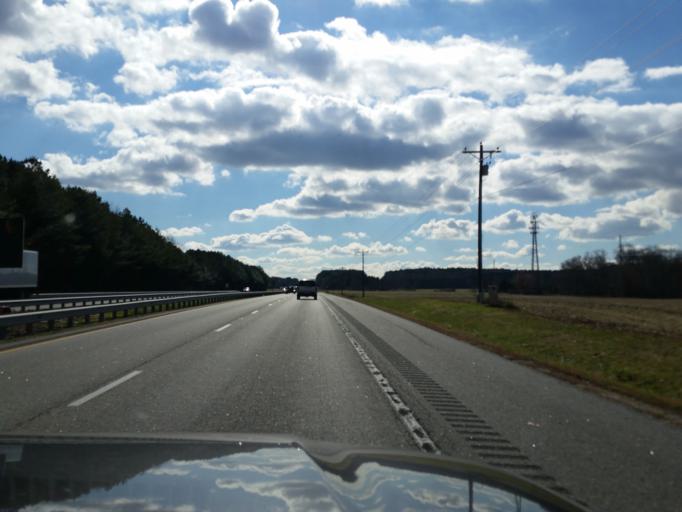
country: US
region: Maryland
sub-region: Talbot County
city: Easton
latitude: 38.8781
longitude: -76.0615
